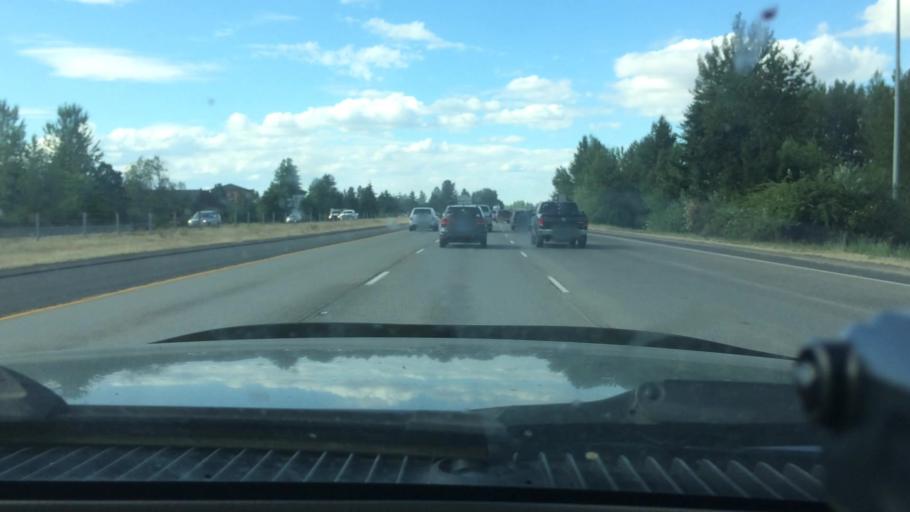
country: US
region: Oregon
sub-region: Marion County
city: Four Corners
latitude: 44.9210
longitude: -122.9899
